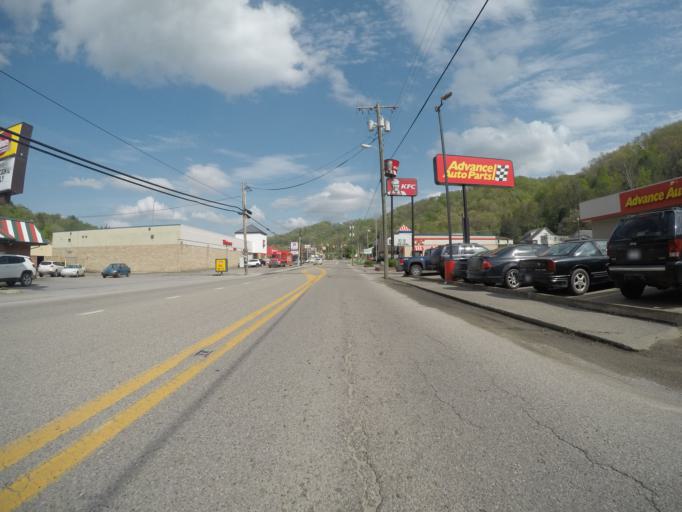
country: US
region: West Virginia
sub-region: Boone County
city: Madison
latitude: 38.0800
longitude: -81.8334
